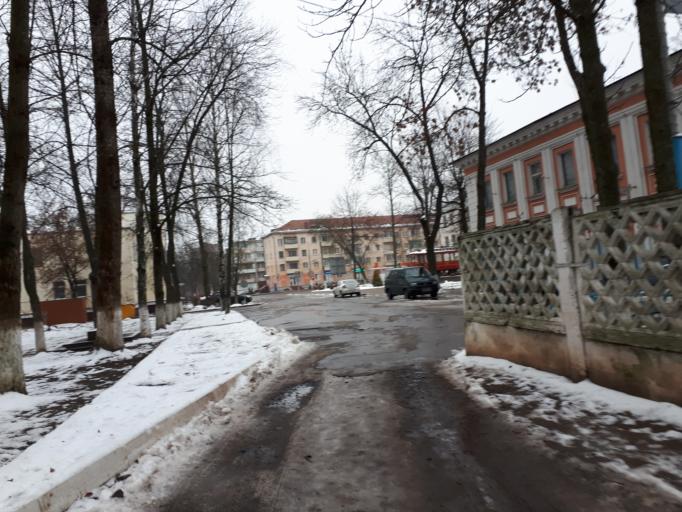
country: BY
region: Vitebsk
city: Vitebsk
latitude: 55.1920
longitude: 30.2209
